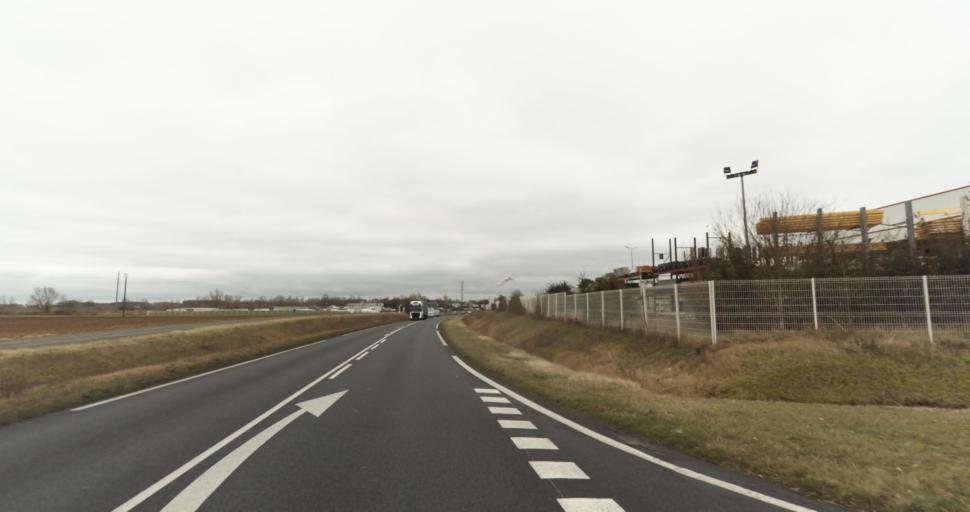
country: FR
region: Pays de la Loire
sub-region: Departement de Maine-et-Loire
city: Doue-la-Fontaine
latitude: 47.1881
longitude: -0.2433
